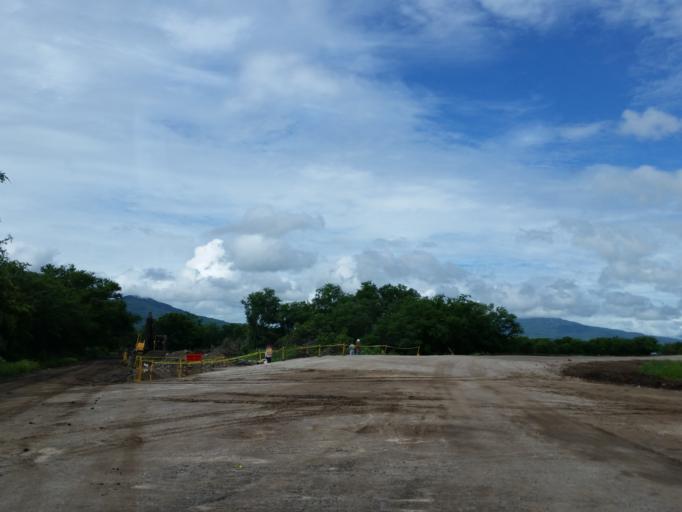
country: NI
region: Leon
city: Larreynaga
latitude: 12.5895
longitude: -86.6695
